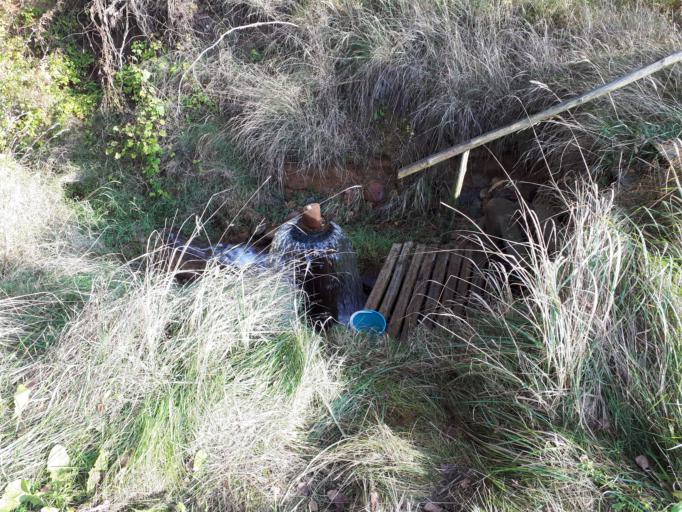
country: LT
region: Alytaus apskritis
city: Druskininkai
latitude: 54.2078
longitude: 23.9589
